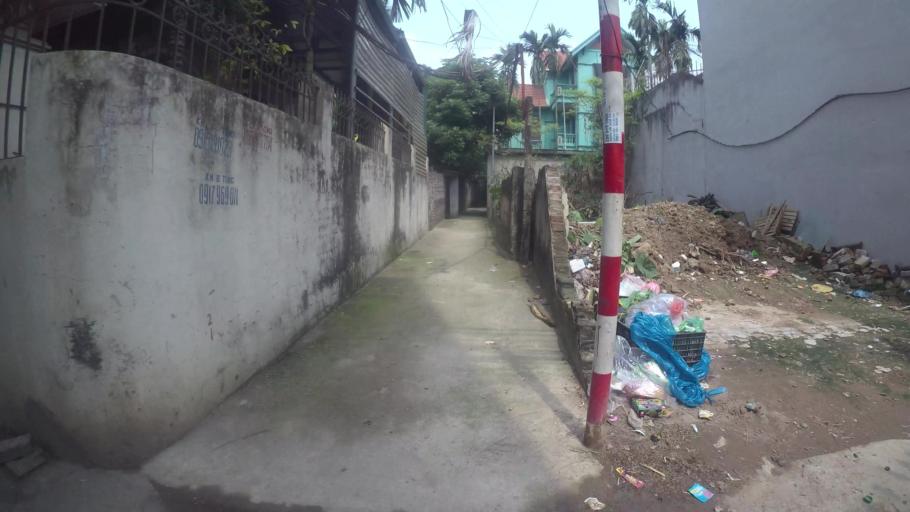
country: VN
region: Ha Noi
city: Tay Ho
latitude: 21.0880
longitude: 105.8002
